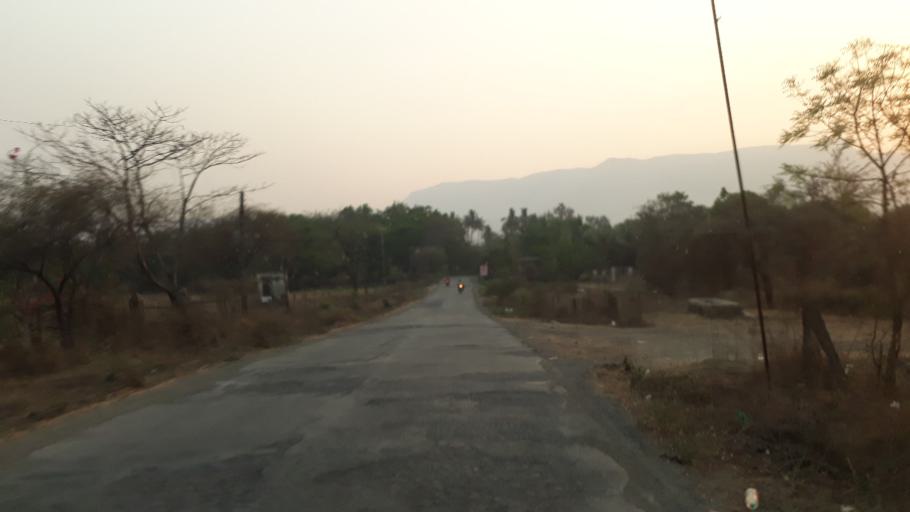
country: IN
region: Maharashtra
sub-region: Raigarh
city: Neral
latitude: 19.0398
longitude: 73.3300
